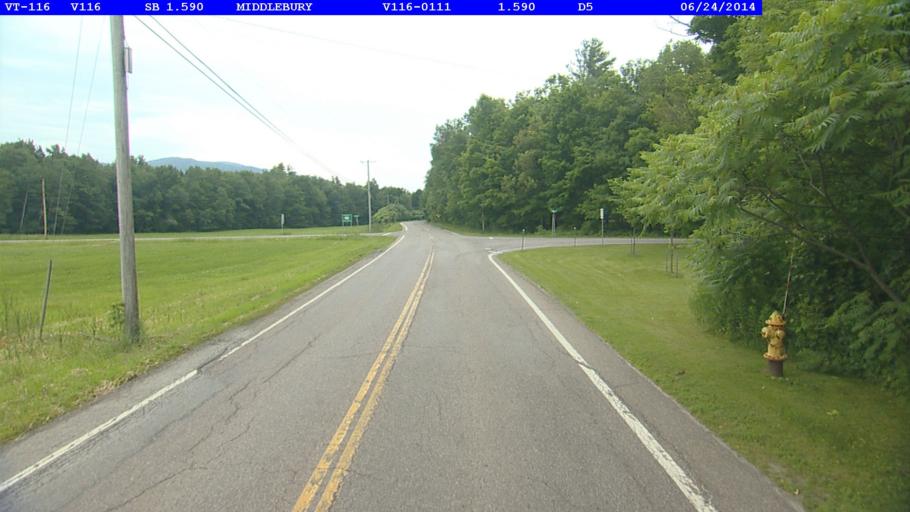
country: US
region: Vermont
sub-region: Addison County
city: Middlebury (village)
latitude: 43.9874
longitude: -73.1046
